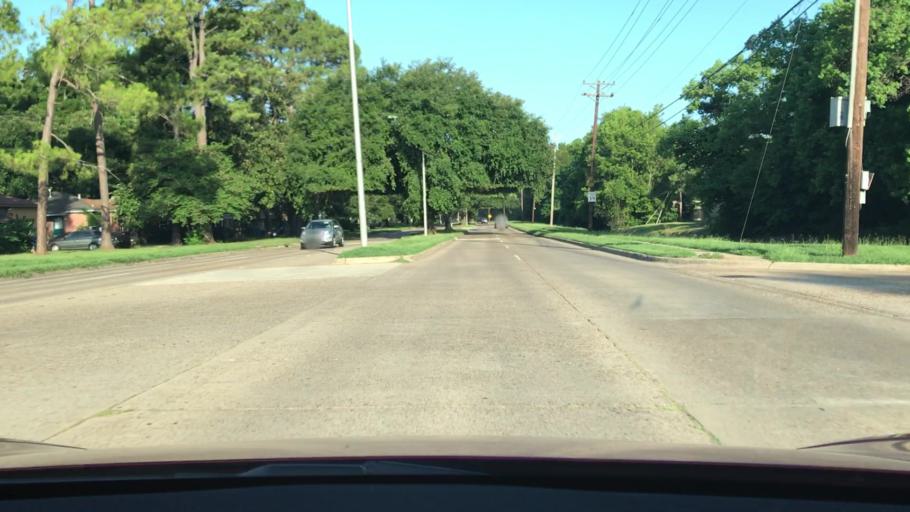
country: US
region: Louisiana
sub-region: Bossier Parish
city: Bossier City
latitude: 32.4567
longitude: -93.7246
